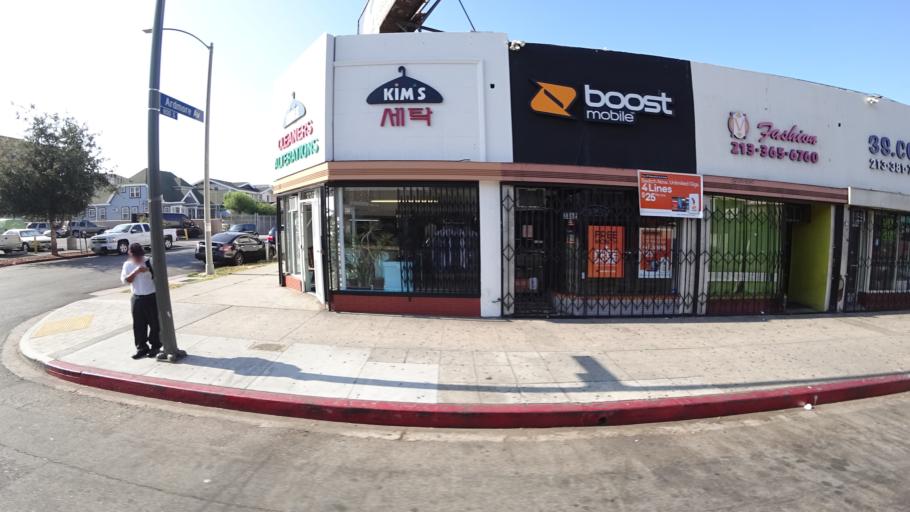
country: US
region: California
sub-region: Los Angeles County
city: Silver Lake
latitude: 34.0576
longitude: -118.3023
